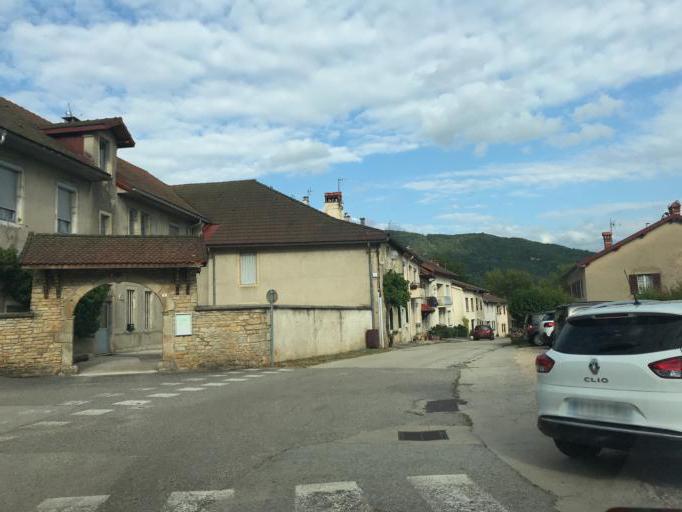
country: FR
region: Franche-Comte
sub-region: Departement du Jura
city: Saint-Lupicin
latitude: 46.4011
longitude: 5.7941
